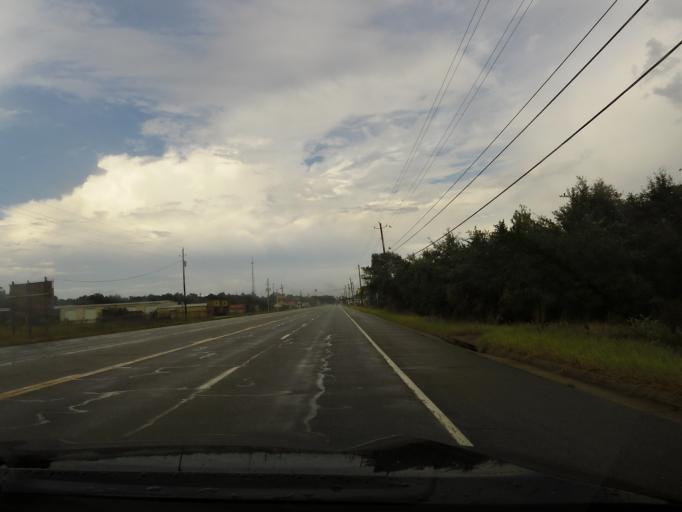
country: US
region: Georgia
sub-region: Wayne County
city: Jesup
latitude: 31.6520
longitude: -81.8533
